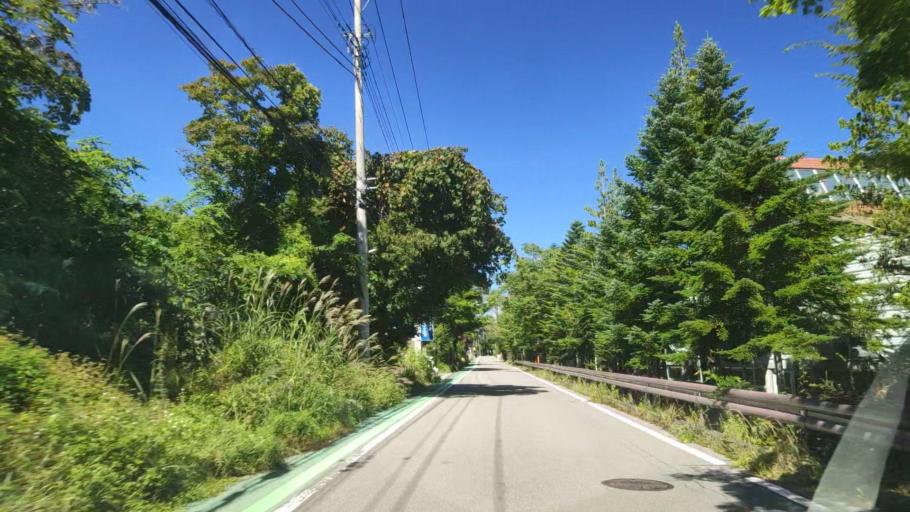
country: JP
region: Shizuoka
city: Gotemba
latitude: 35.4145
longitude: 138.8540
